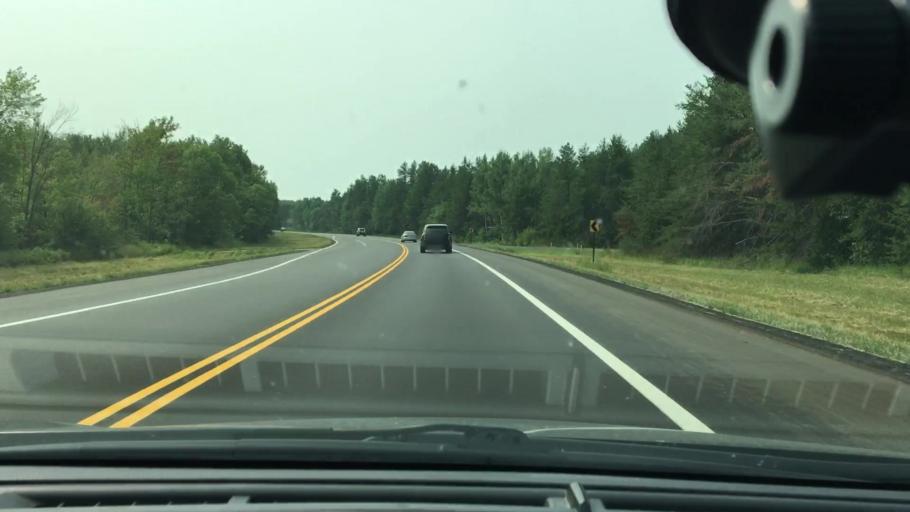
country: US
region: Minnesota
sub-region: Crow Wing County
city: Brainerd
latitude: 46.4250
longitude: -94.1779
